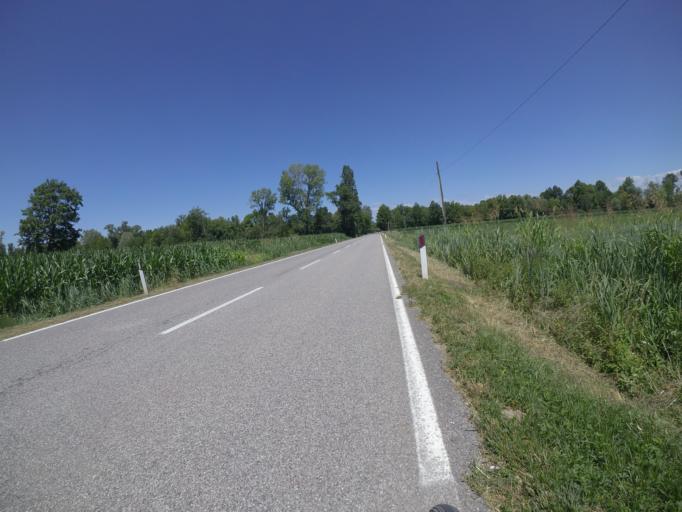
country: IT
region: Friuli Venezia Giulia
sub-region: Provincia di Udine
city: Talmassons
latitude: 45.9189
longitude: 13.0848
